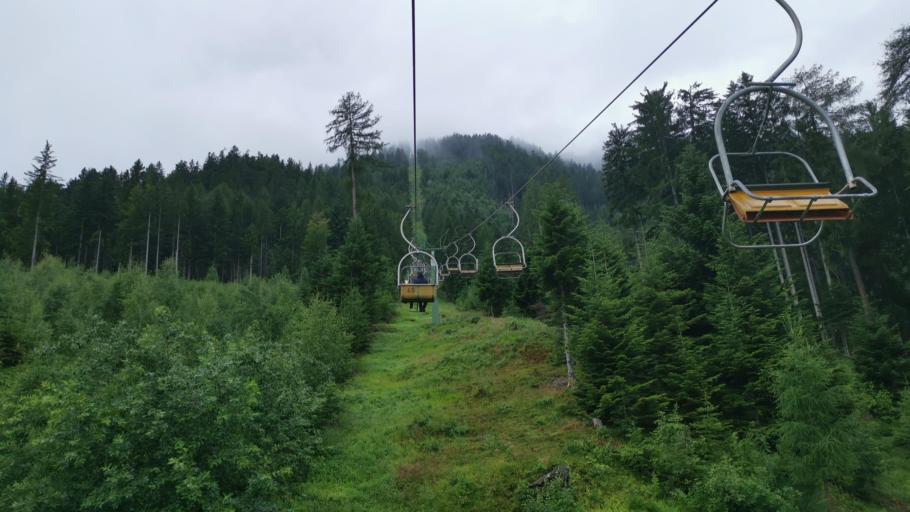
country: AT
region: Tyrol
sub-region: Politischer Bezirk Lienz
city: Leisach
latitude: 46.8250
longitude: 12.7385
